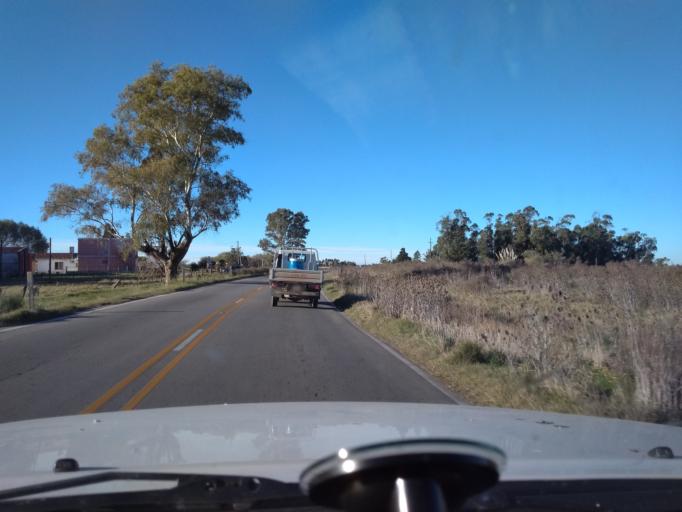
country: UY
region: Canelones
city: San Bautista
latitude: -34.4612
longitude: -56.0029
